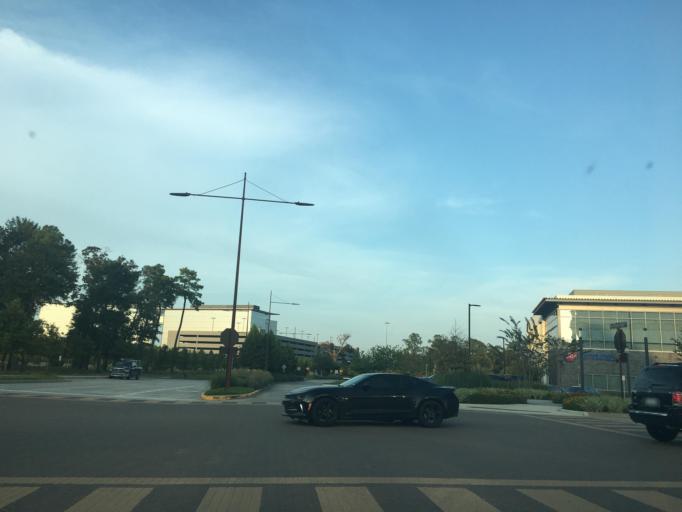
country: US
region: Texas
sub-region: Harris County
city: Spring
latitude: 30.0965
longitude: -95.4407
